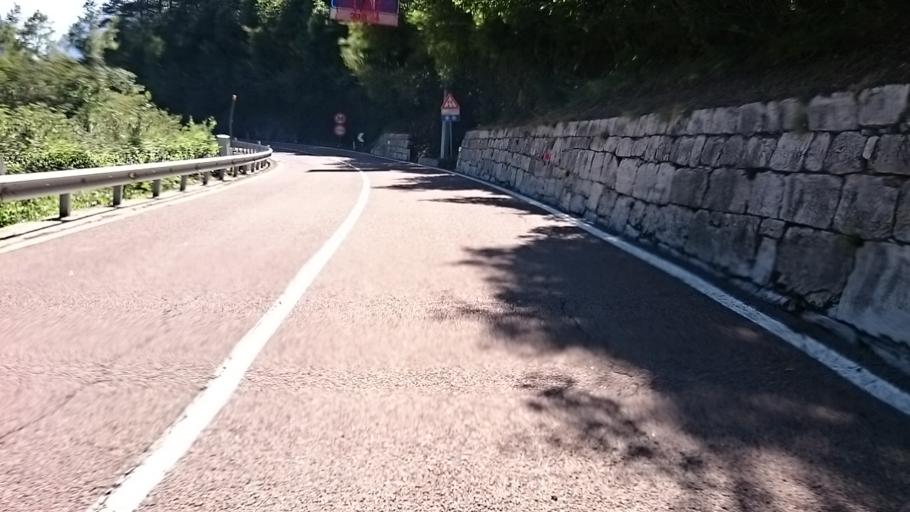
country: IT
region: Veneto
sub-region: Provincia di Belluno
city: Perarolo di Cadore
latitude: 46.3636
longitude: 12.3461
